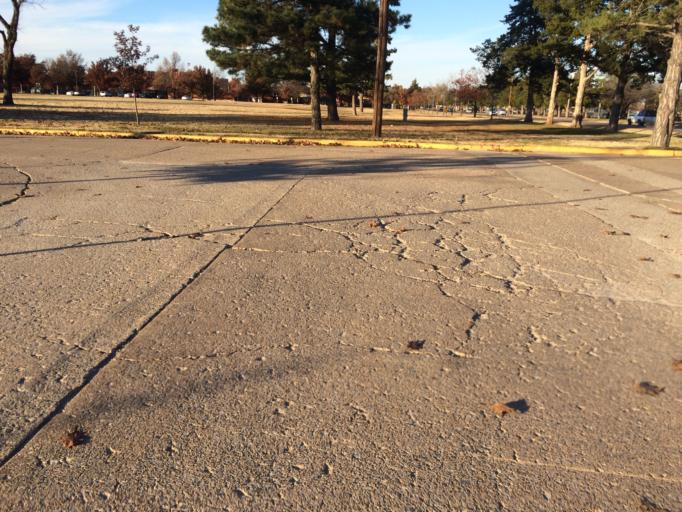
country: US
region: Oklahoma
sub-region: Cleveland County
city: Norman
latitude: 35.1925
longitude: -97.4416
